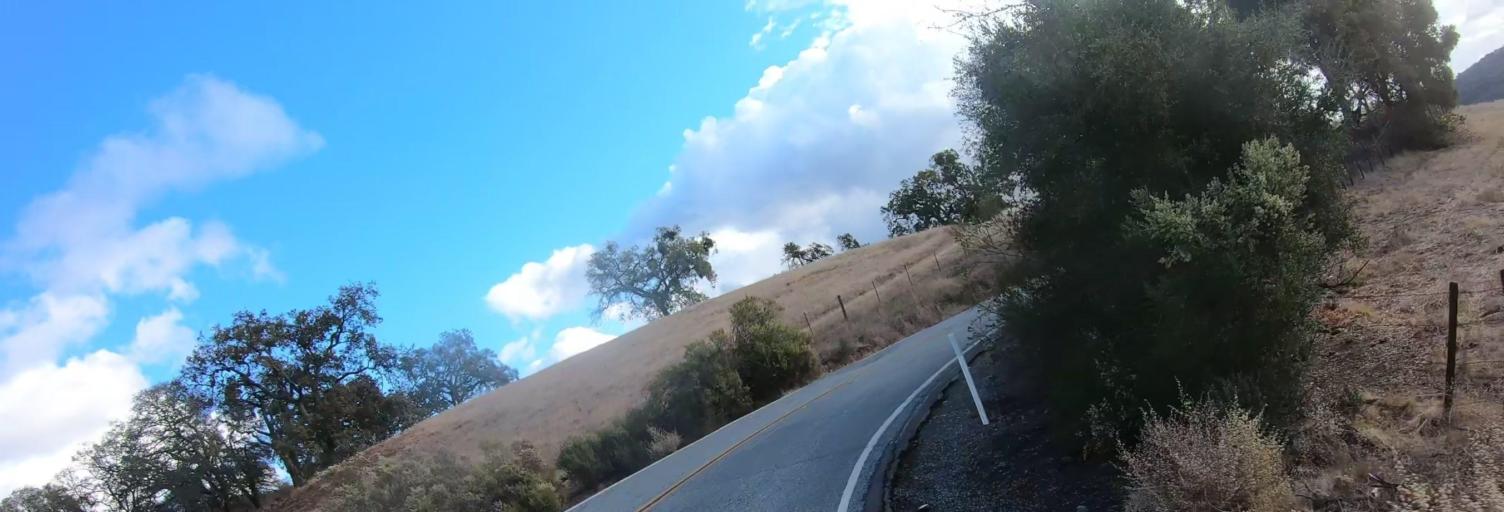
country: US
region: California
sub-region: Santa Clara County
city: East Foothills
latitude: 37.3377
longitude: -121.7073
